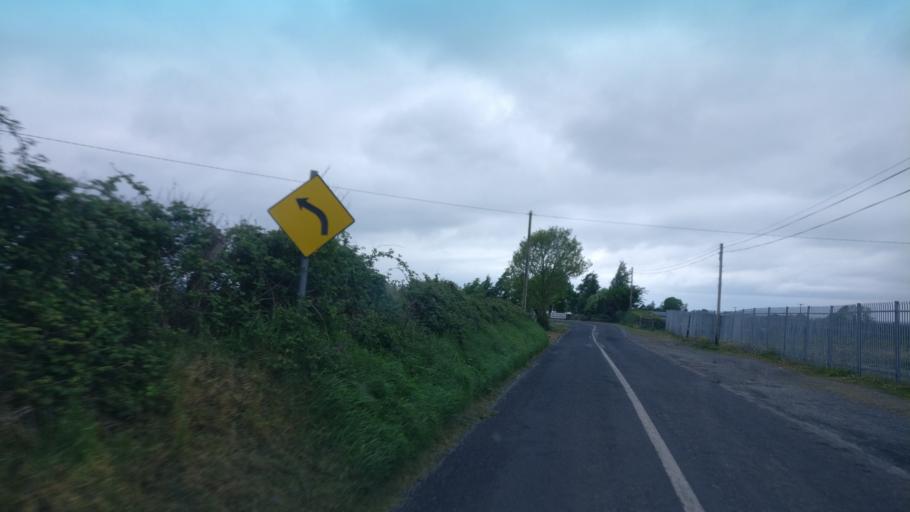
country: IE
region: Connaught
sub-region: County Galway
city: Portumna
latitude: 53.1126
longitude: -8.2773
